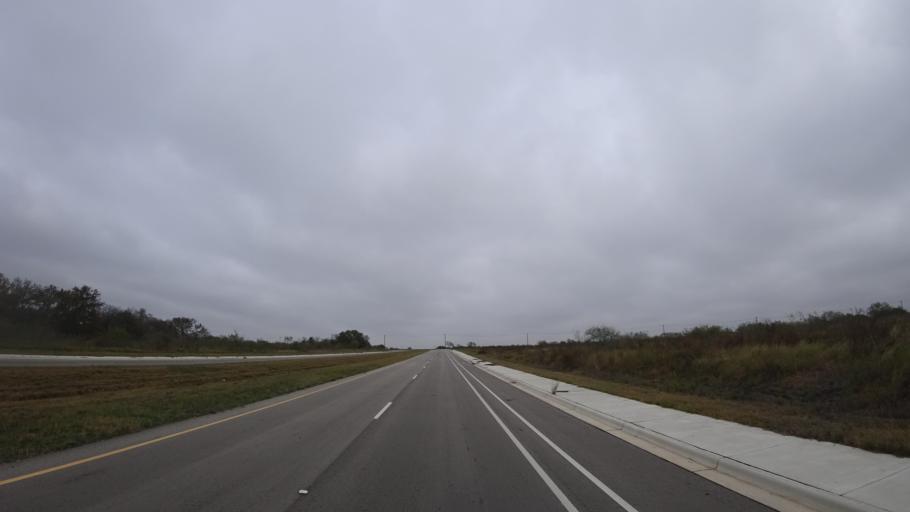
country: US
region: Texas
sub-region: Travis County
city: Pflugerville
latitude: 30.4126
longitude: -97.6121
